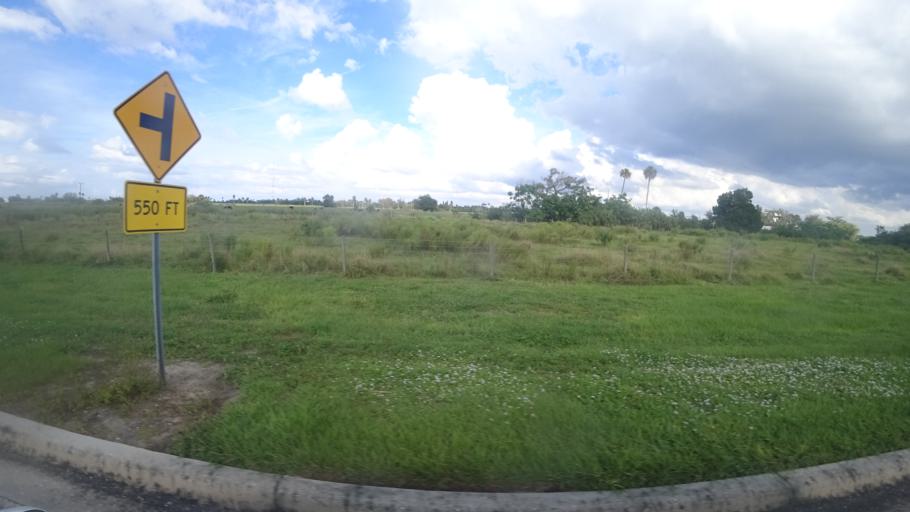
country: US
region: Florida
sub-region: Manatee County
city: Palmetto
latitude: 27.5342
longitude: -82.5766
